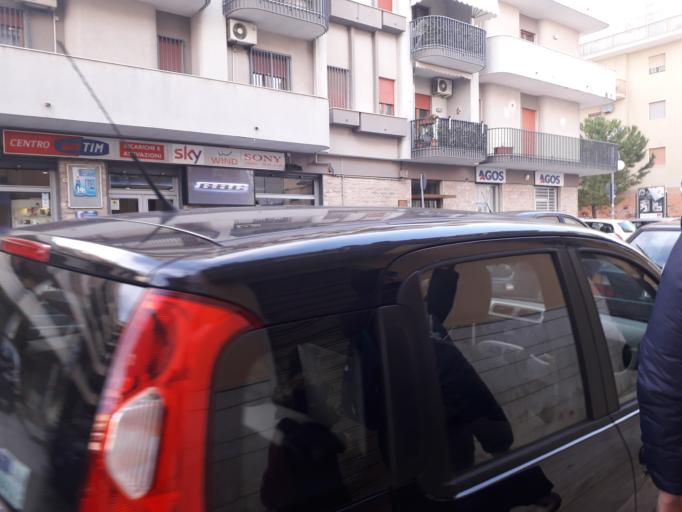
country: IT
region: Apulia
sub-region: Provincia di Barletta - Andria - Trani
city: Andria
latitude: 41.2316
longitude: 16.2986
